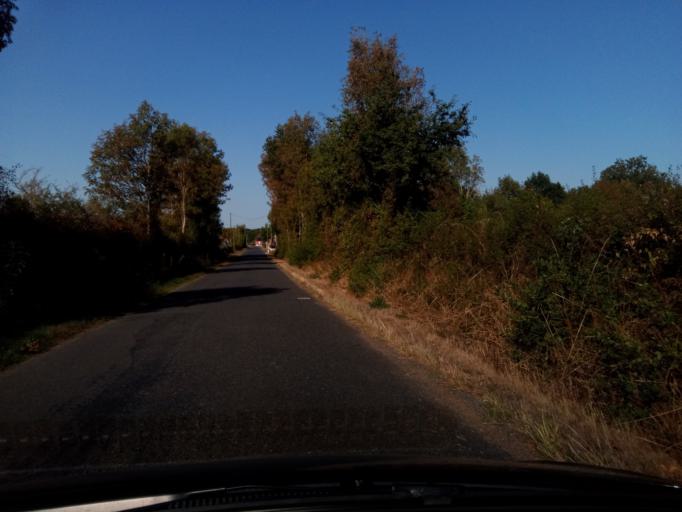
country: FR
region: Poitou-Charentes
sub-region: Departement de la Vienne
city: Saulge
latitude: 46.3295
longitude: 0.8397
